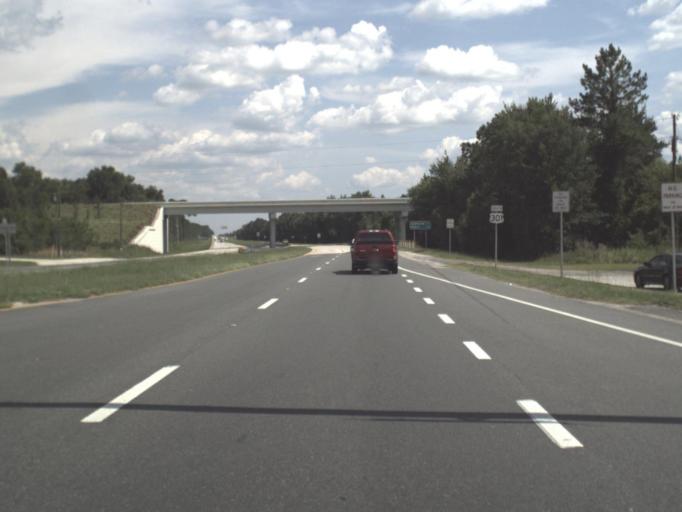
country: US
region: Florida
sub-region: Alachua County
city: Waldo
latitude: 29.7167
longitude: -82.1399
